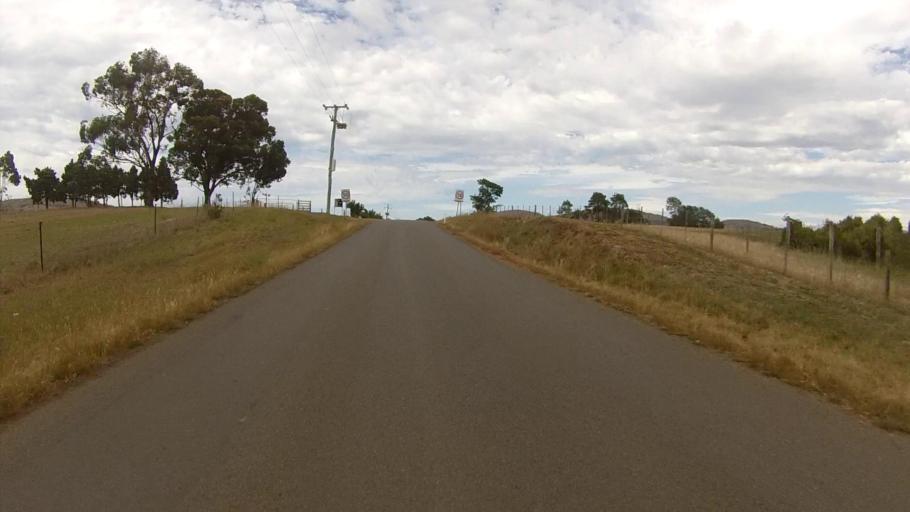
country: AU
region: Tasmania
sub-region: Clarence
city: Cambridge
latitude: -42.7284
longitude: 147.4492
